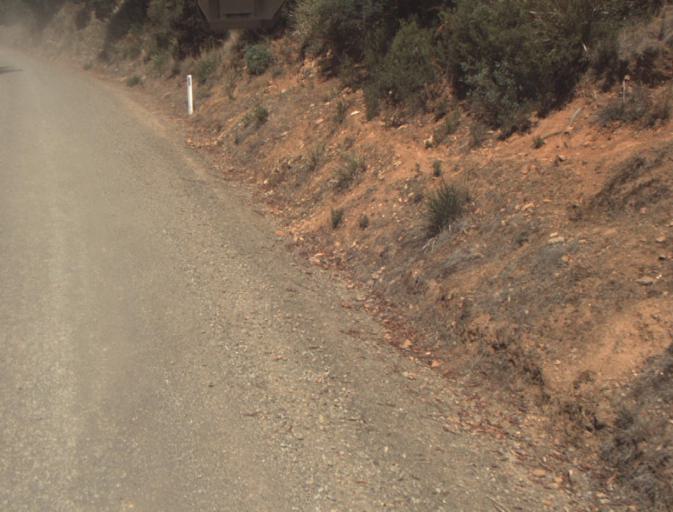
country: AU
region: Tasmania
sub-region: Dorset
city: Scottsdale
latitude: -41.3078
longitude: 147.3695
